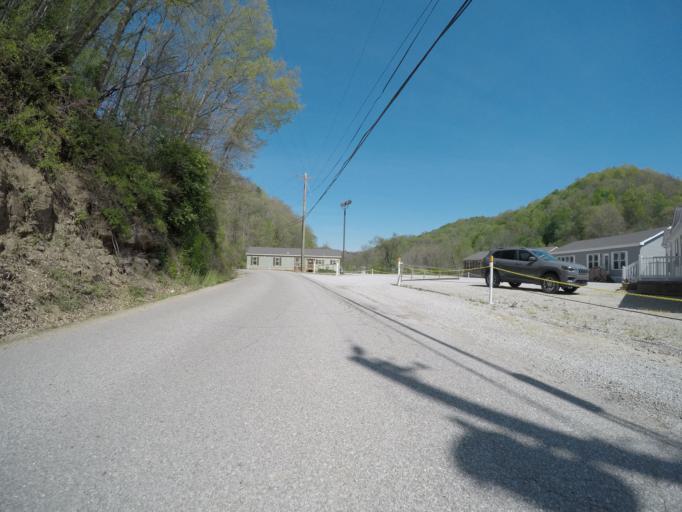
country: US
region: West Virginia
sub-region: Kanawha County
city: Charleston
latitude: 38.4129
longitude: -81.6258
